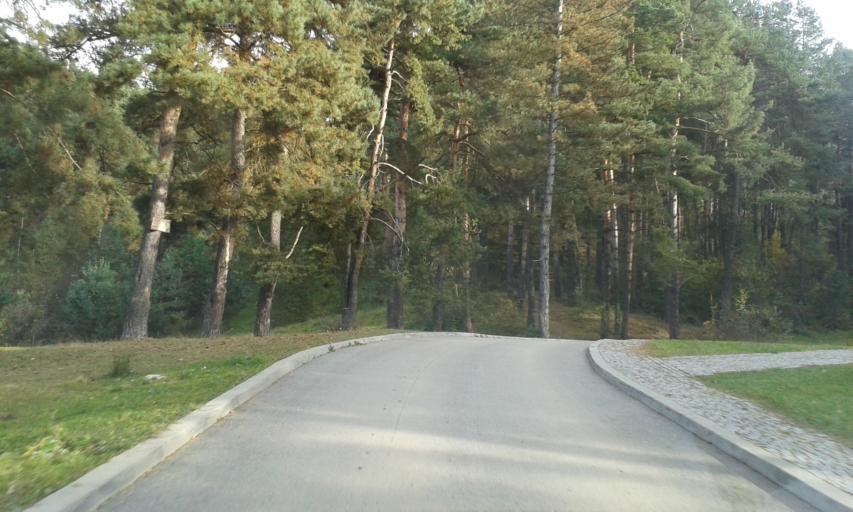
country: RO
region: Hunedoara
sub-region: Municipiul Petrosani
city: Petrosani
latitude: 45.4213
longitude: 23.3822
